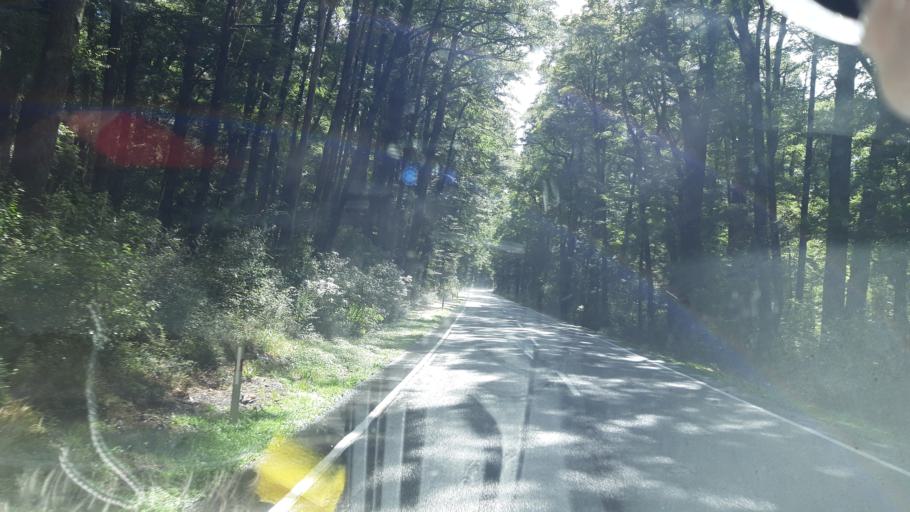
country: NZ
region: Canterbury
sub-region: Hurunui District
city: Amberley
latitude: -42.3779
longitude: 172.2764
